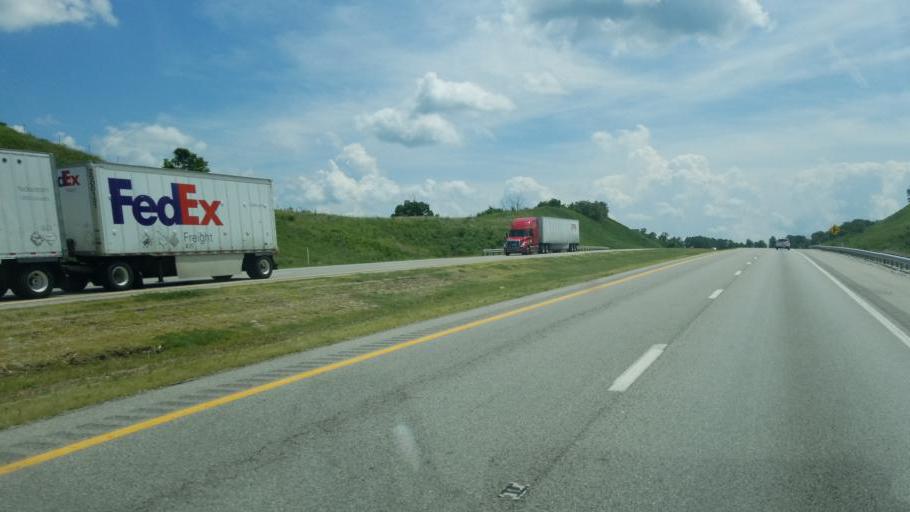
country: US
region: West Virginia
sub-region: Mason County
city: Point Pleasant
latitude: 38.7953
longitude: -82.0970
